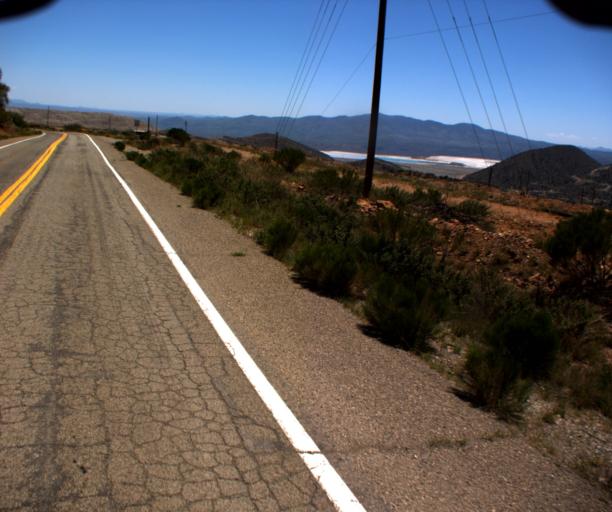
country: US
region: Arizona
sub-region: Greenlee County
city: Morenci
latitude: 33.0709
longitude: -109.3756
